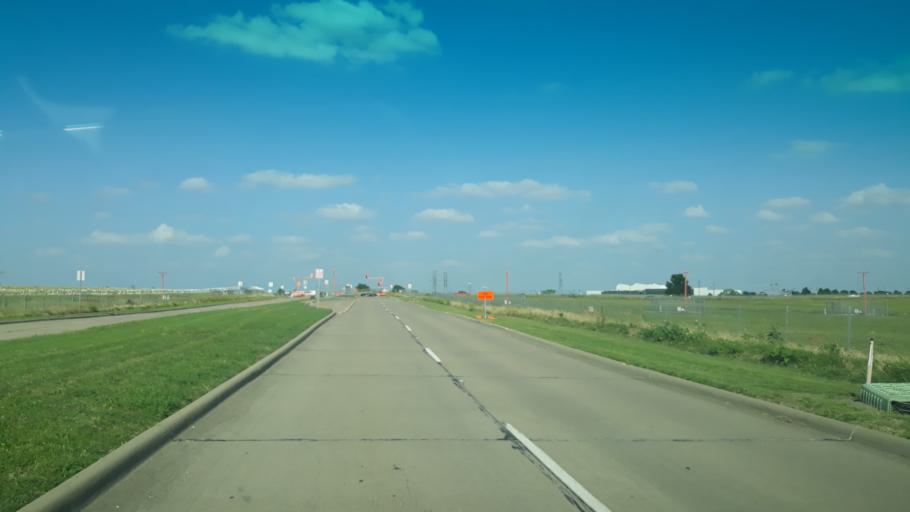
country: US
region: Texas
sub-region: Tarrant County
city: Euless
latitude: 32.8695
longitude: -97.0114
